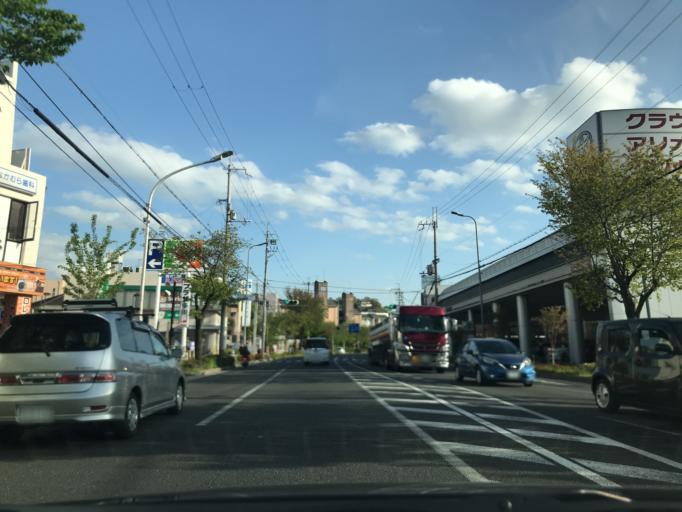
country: JP
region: Osaka
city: Ikeda
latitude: 34.8588
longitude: 135.4163
